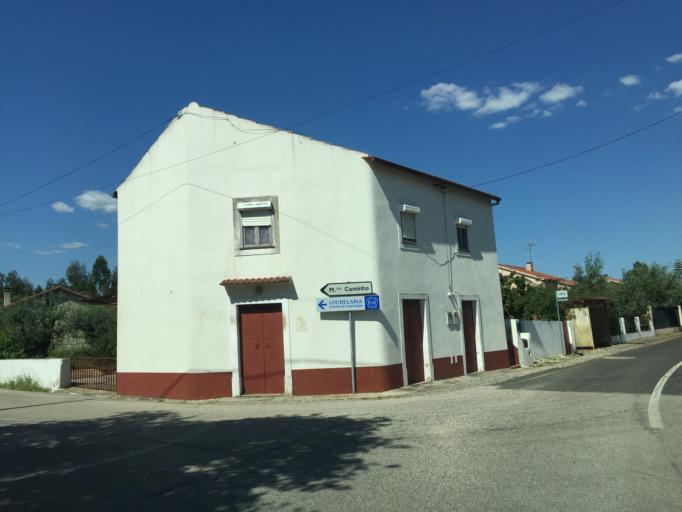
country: PT
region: Leiria
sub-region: Alvaiazere
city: Alvaiazere
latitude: 39.8345
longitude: -8.3818
